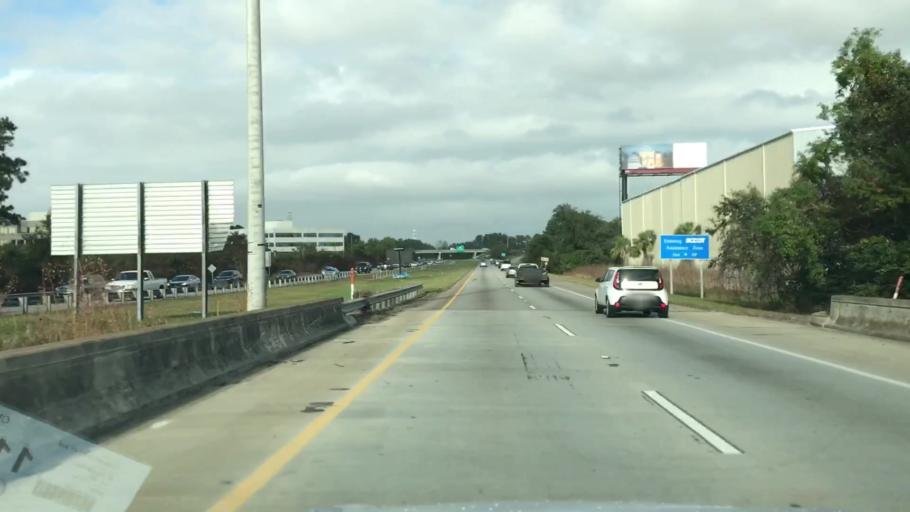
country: US
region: South Carolina
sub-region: Charleston County
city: North Charleston
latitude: 32.8373
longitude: -80.0226
